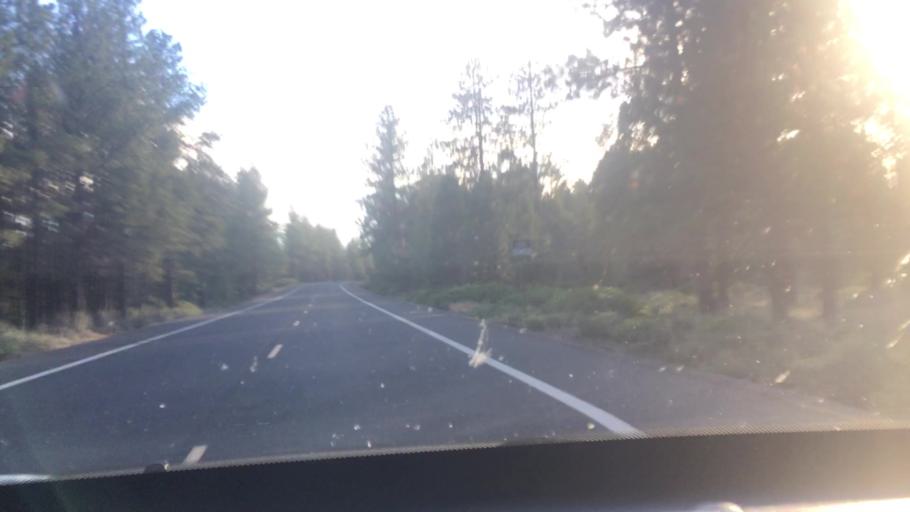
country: US
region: Oregon
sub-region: Deschutes County
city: Deschutes River Woods
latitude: 44.0451
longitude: -121.4027
